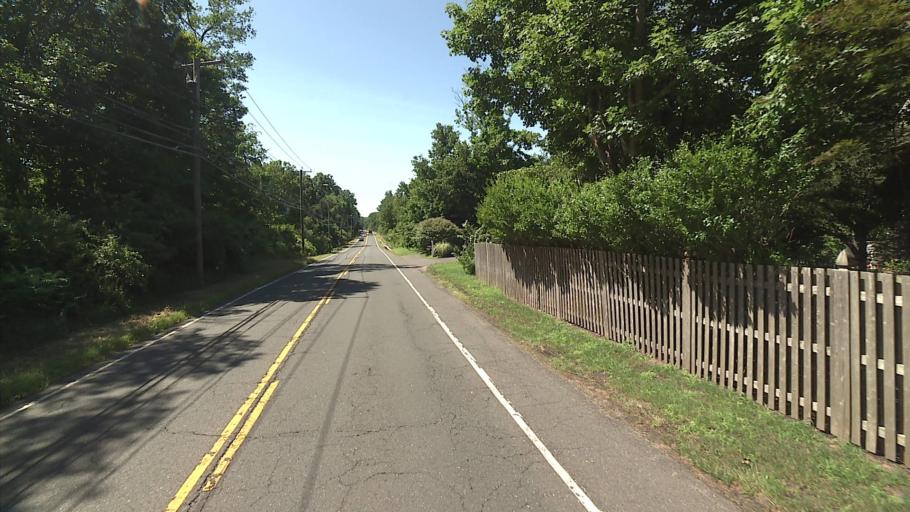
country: US
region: Connecticut
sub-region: Hartford County
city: Farmington
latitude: 41.7538
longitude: -72.8187
